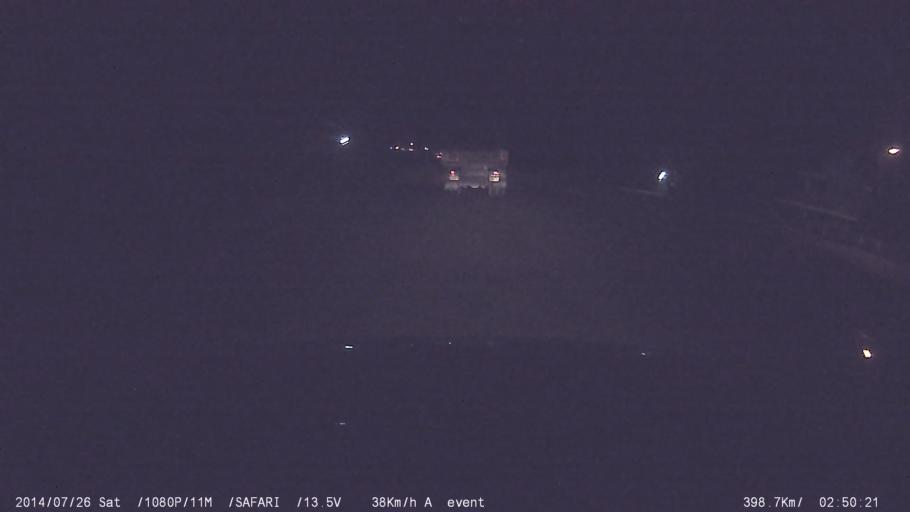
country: IN
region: Kerala
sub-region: Palakkad district
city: Palakkad
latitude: 10.7543
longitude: 76.6636
